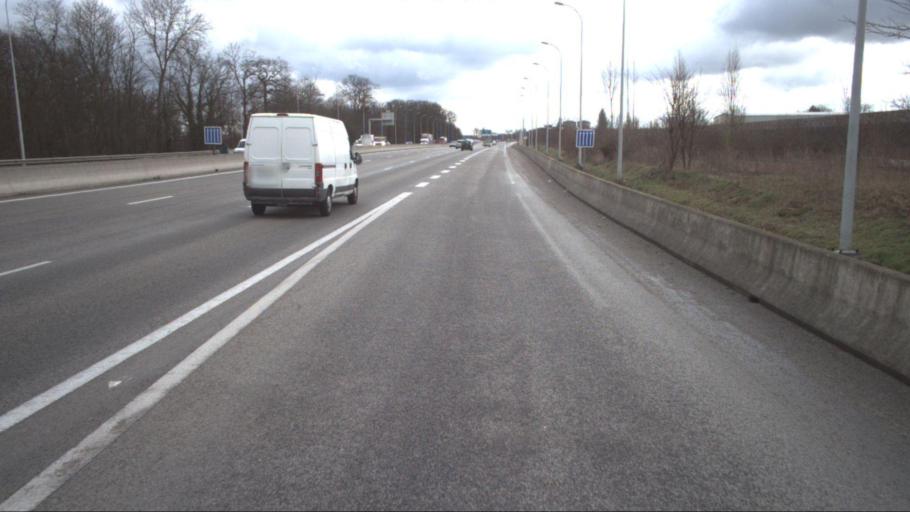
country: FR
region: Ile-de-France
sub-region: Departement des Yvelines
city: Buc
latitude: 48.7906
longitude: 2.1093
